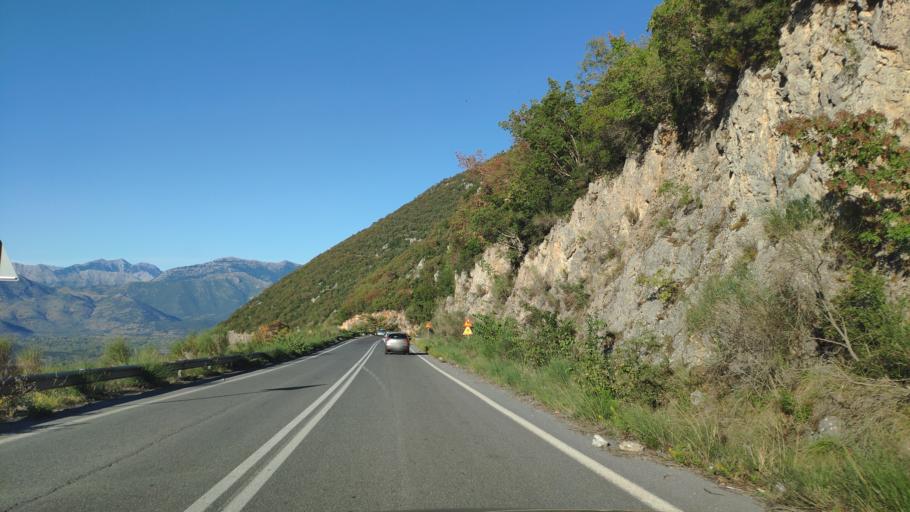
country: GR
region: Peloponnese
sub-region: Nomos Arkadias
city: Langadhia
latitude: 37.7161
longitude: 22.1996
